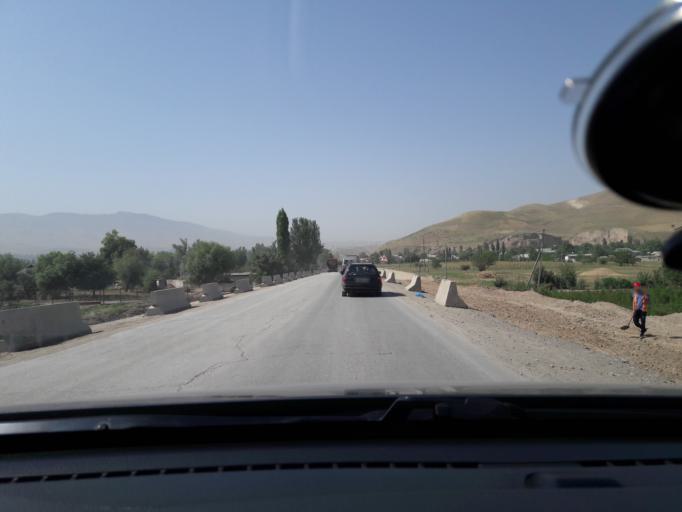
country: TJ
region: Dushanbe
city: Boshkengash
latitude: 38.4500
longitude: 68.7344
